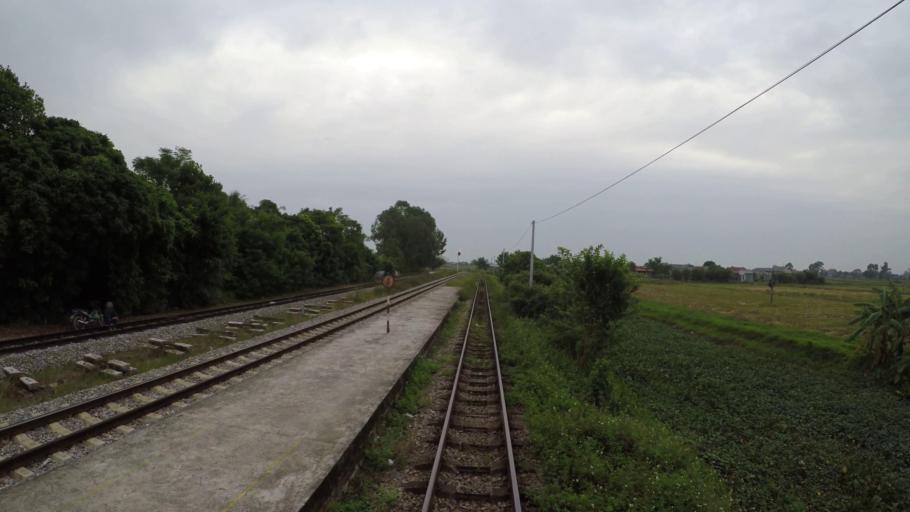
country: VN
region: Hai Duong
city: Ke Sat
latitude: 20.9673
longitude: 106.1655
